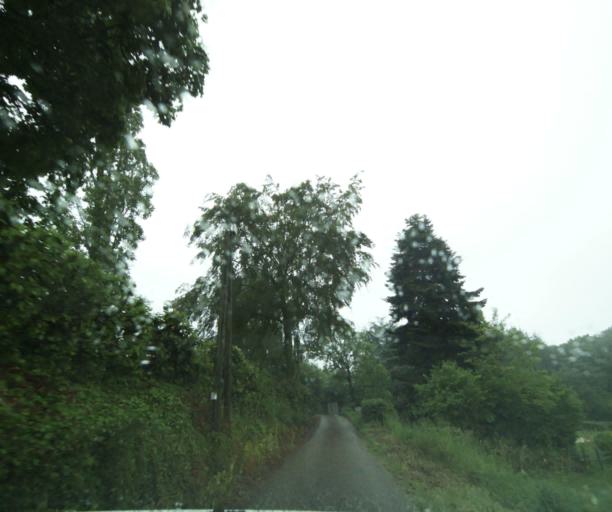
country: FR
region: Bourgogne
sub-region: Departement de Saone-et-Loire
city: La Clayette
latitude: 46.3642
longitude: 4.3503
